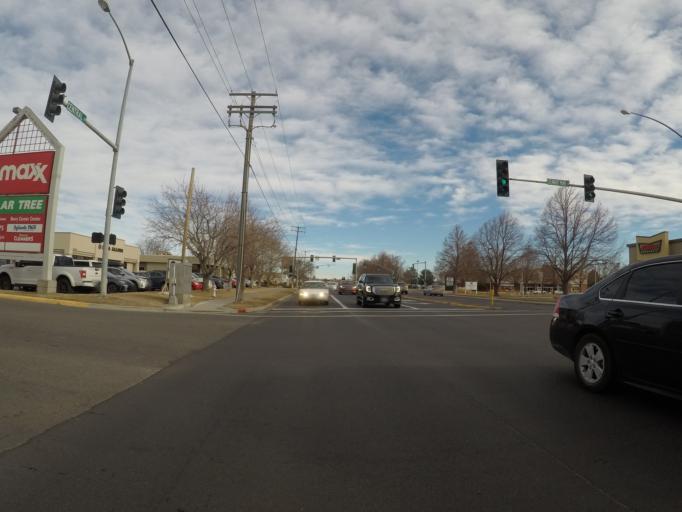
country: US
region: Montana
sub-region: Yellowstone County
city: Billings
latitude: 45.7698
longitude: -108.5817
